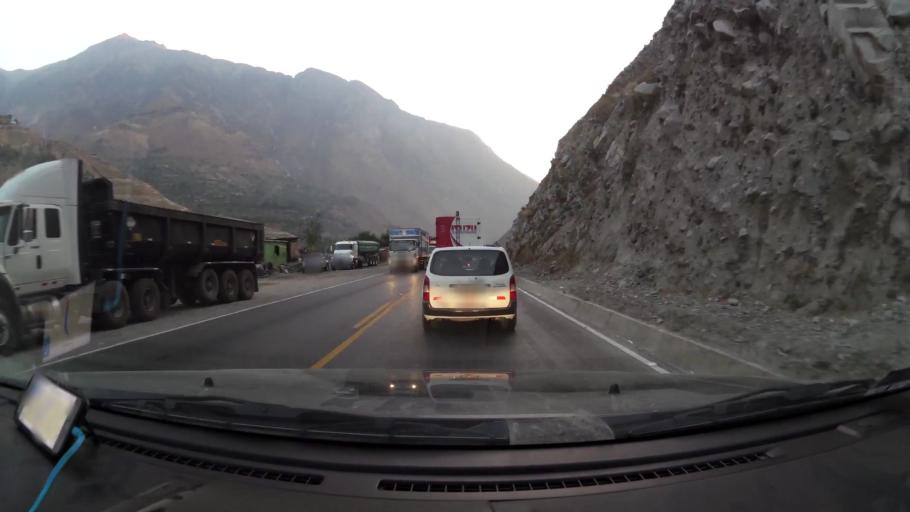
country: PE
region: Lima
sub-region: Provincia de Huarochiri
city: Surco
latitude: -11.8817
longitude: -76.4384
